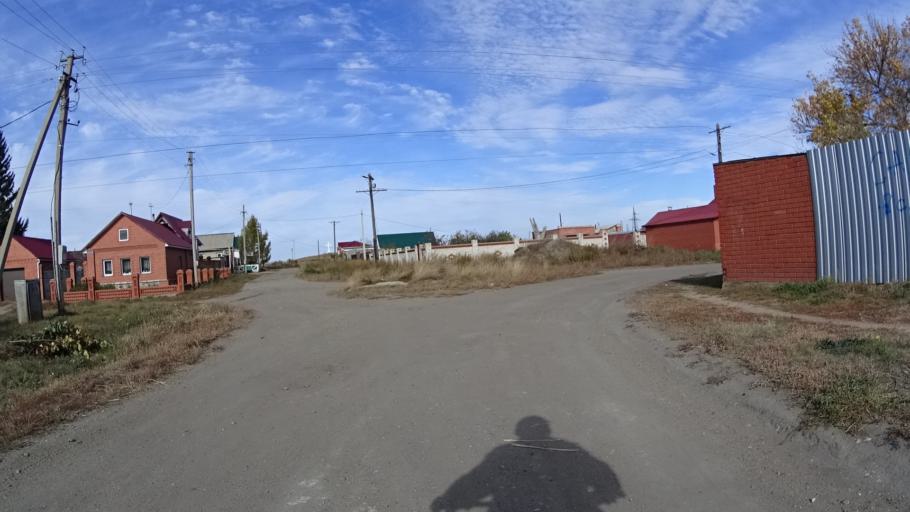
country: RU
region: Chelyabinsk
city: Troitsk
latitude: 54.0760
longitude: 61.5821
